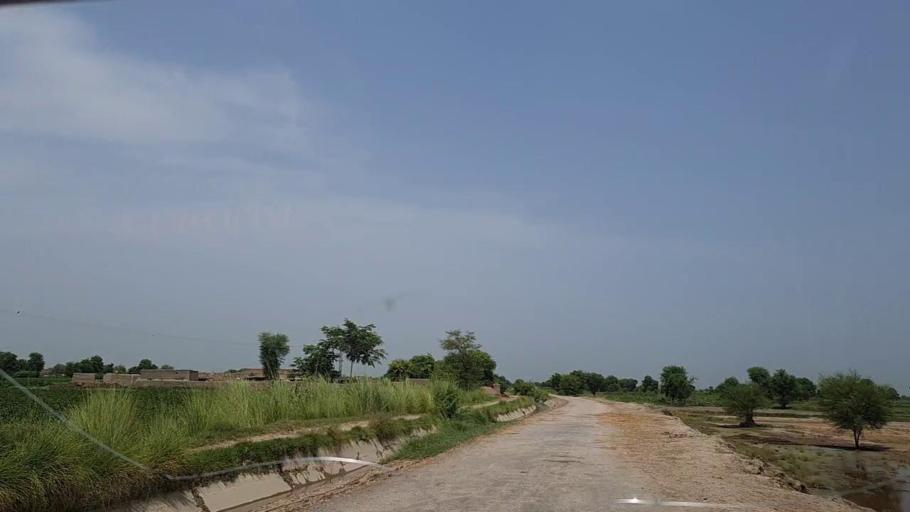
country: PK
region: Sindh
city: Tharu Shah
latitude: 26.9271
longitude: 68.0681
